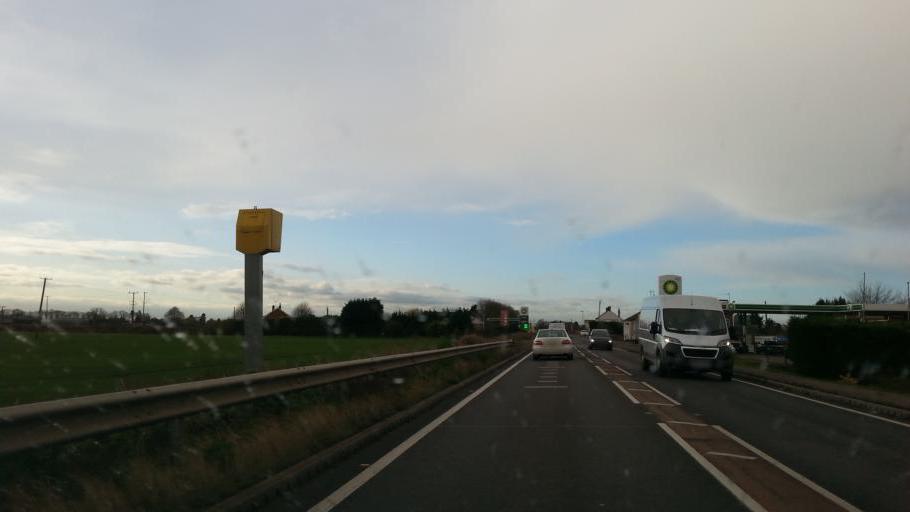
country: GB
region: England
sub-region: Peterborough
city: Thorney
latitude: 52.6165
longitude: -0.0172
